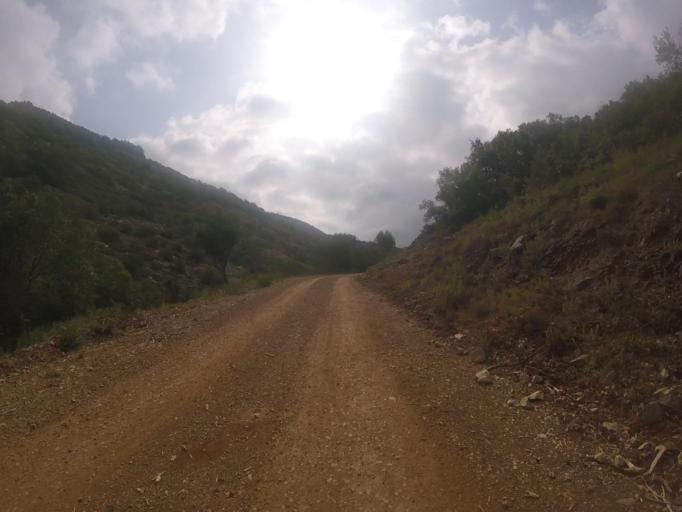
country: ES
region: Valencia
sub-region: Provincia de Castello
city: Santa Magdalena de Pulpis
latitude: 40.3471
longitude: 0.3151
